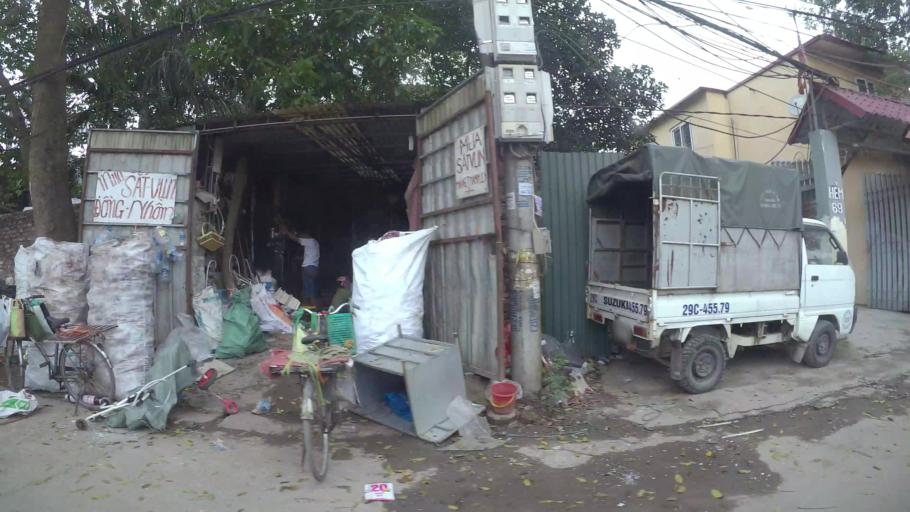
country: VN
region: Ha Noi
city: Tay Ho
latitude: 21.0589
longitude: 105.8393
